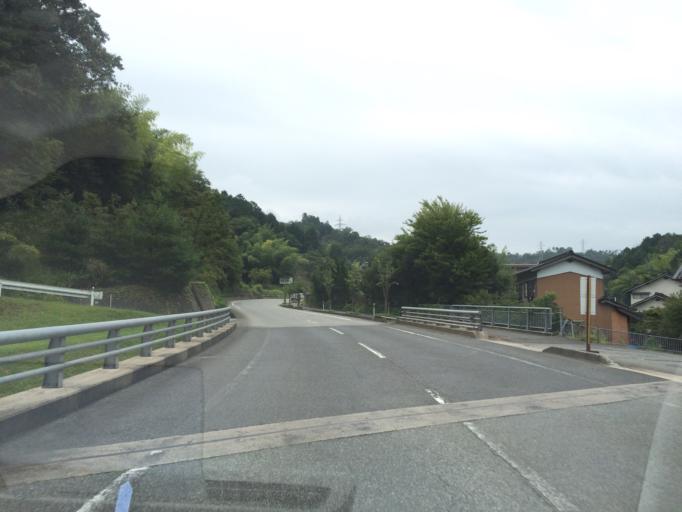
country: JP
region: Hyogo
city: Toyooka
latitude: 35.5309
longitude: 134.8079
